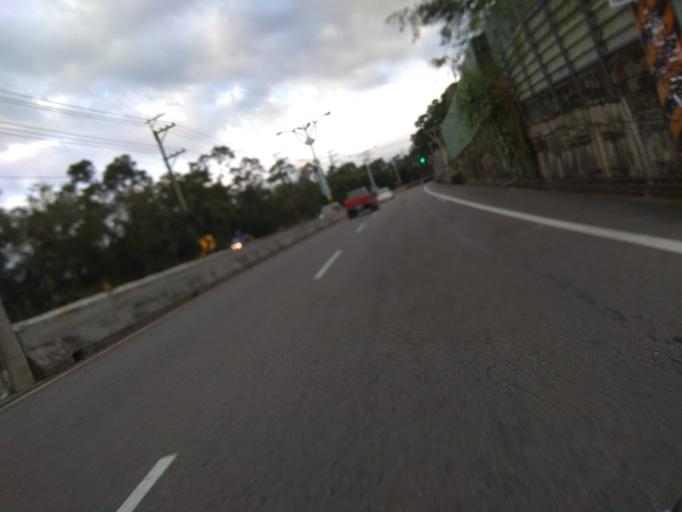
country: TW
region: Taiwan
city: Daxi
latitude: 24.8438
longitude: 121.2110
